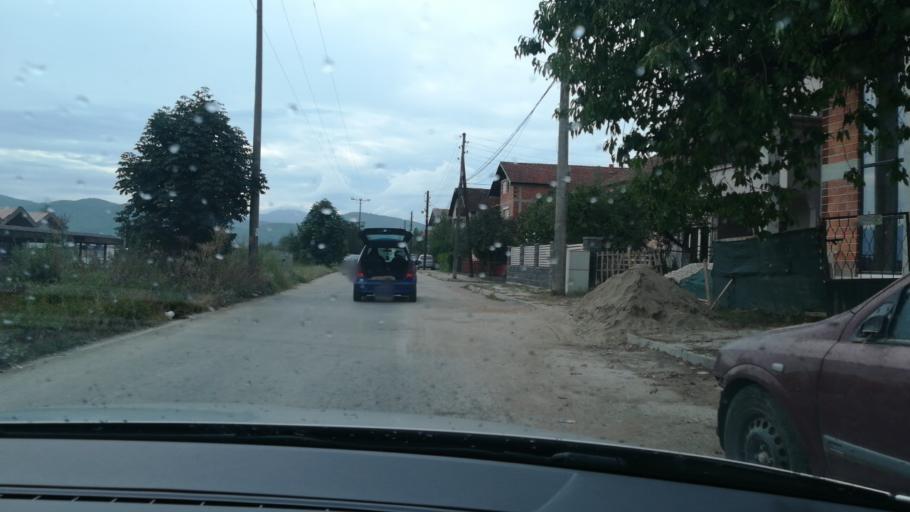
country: MK
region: Kicevo
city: Kicevo
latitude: 41.5136
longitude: 20.9496
